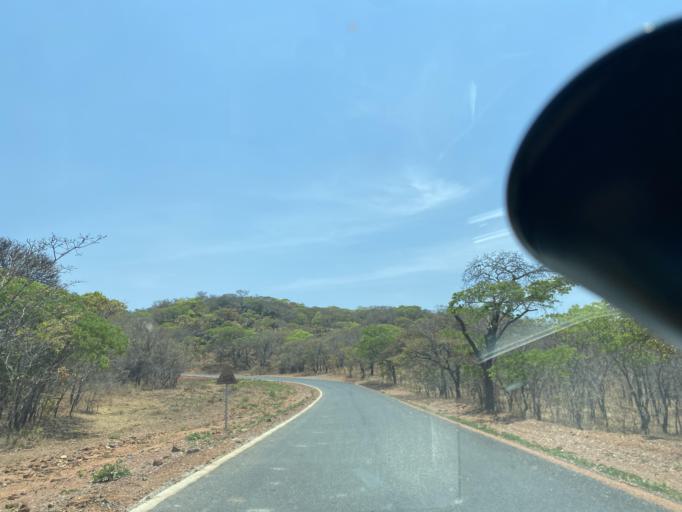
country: ZM
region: Lusaka
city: Kafue
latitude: -15.8602
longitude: 28.4250
